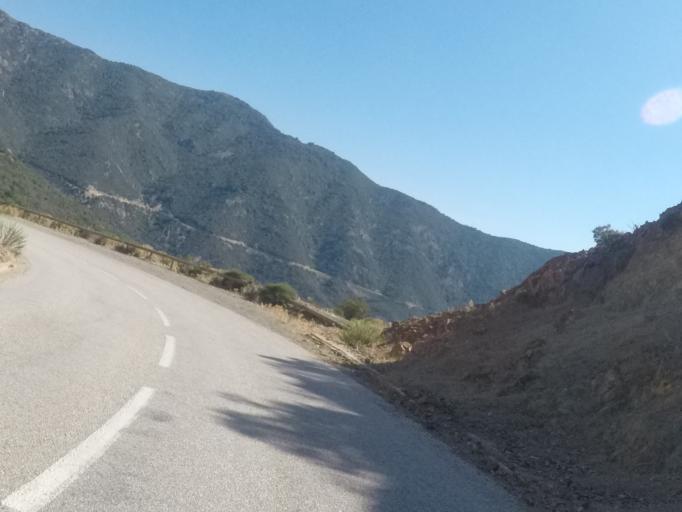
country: FR
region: Corsica
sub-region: Departement de la Corse-du-Sud
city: Cargese
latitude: 42.3517
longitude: 8.6440
